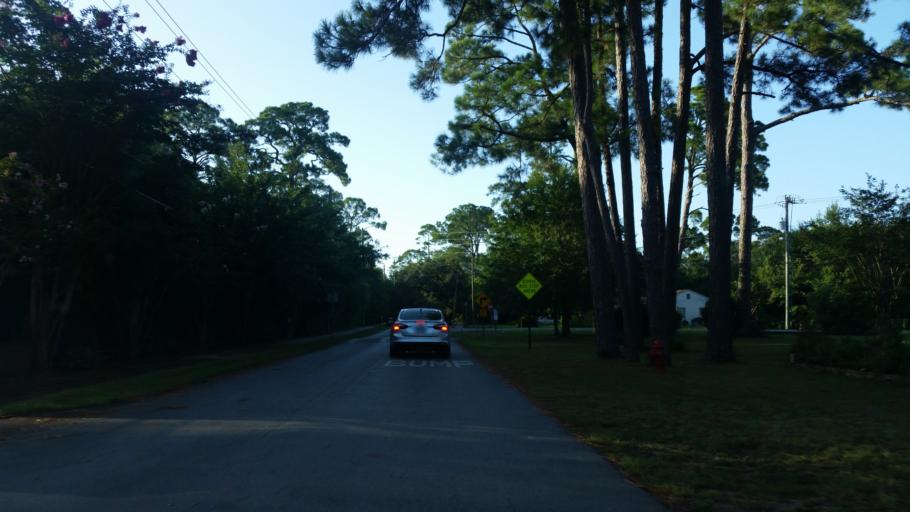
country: US
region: Florida
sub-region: Escambia County
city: Warrington
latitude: 30.3854
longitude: -87.2703
